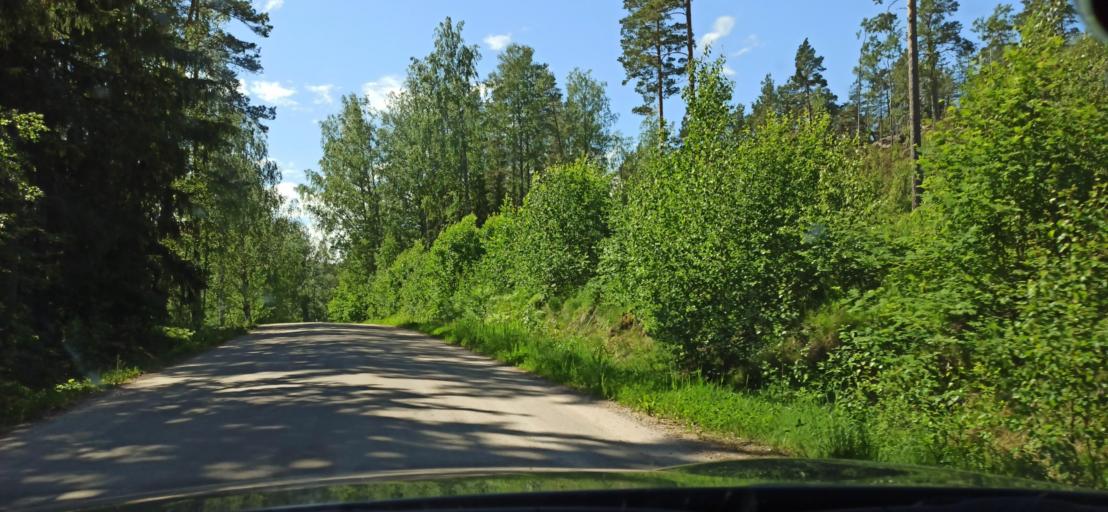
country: FI
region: Varsinais-Suomi
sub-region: Turku
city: Sauvo
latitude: 60.3847
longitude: 22.6545
